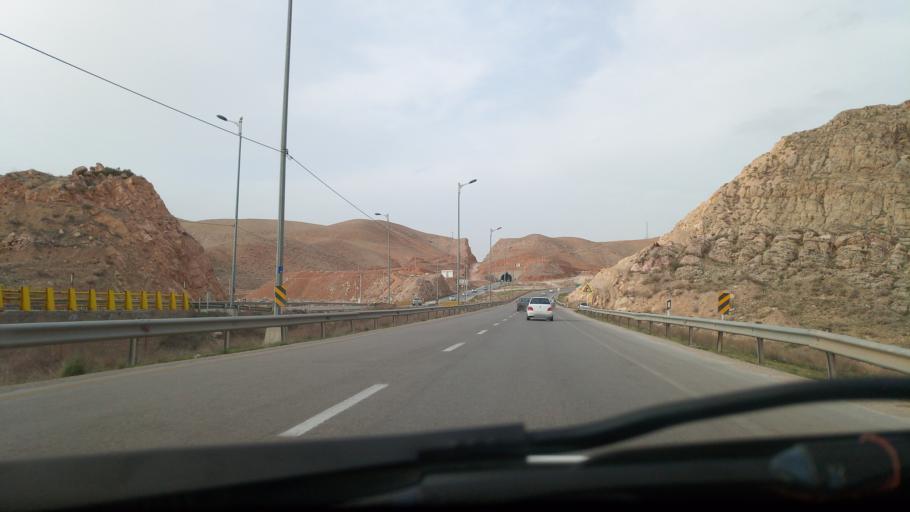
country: IR
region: Khorasan-e Shomali
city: Bojnurd
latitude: 37.4927
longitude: 57.4414
